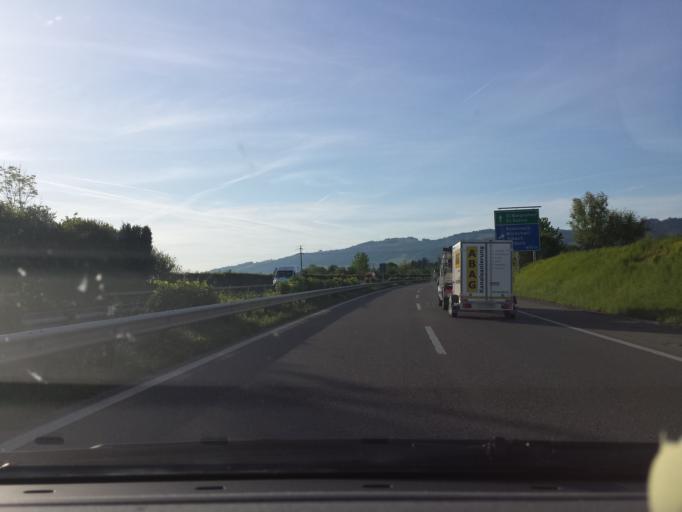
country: CH
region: Saint Gallen
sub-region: Wahlkreis Rorschach
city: Morschwil
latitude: 47.4866
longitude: 9.4387
